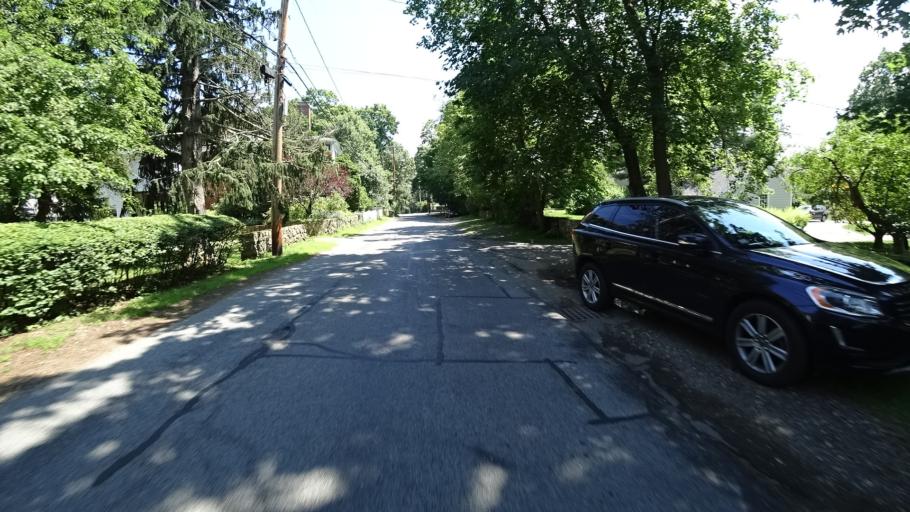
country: US
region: Massachusetts
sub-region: Norfolk County
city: Dedham
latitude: 42.2503
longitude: -71.1897
